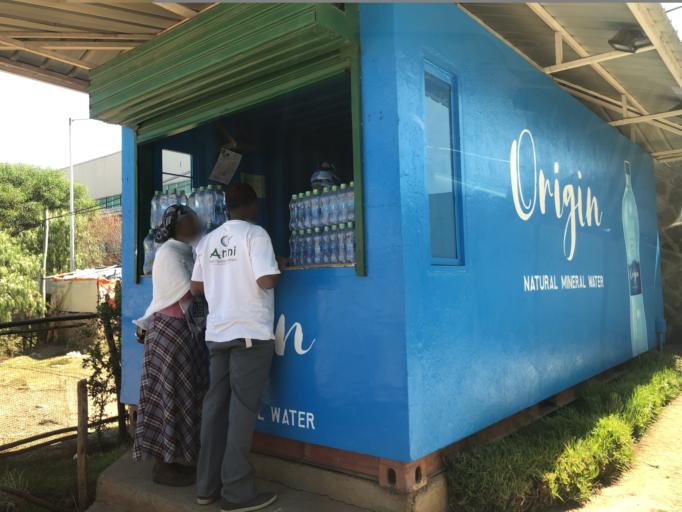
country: ET
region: Oromiya
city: Sebeta
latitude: 8.9123
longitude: 38.6579
